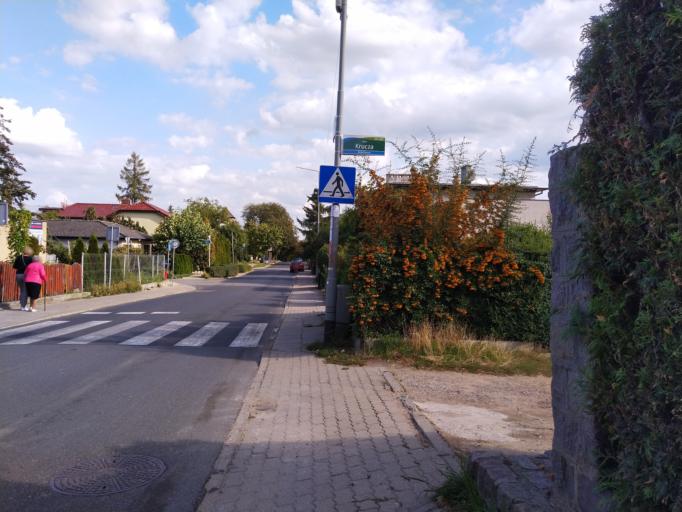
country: PL
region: West Pomeranian Voivodeship
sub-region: Szczecin
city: Szczecin
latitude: 53.4635
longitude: 14.5670
